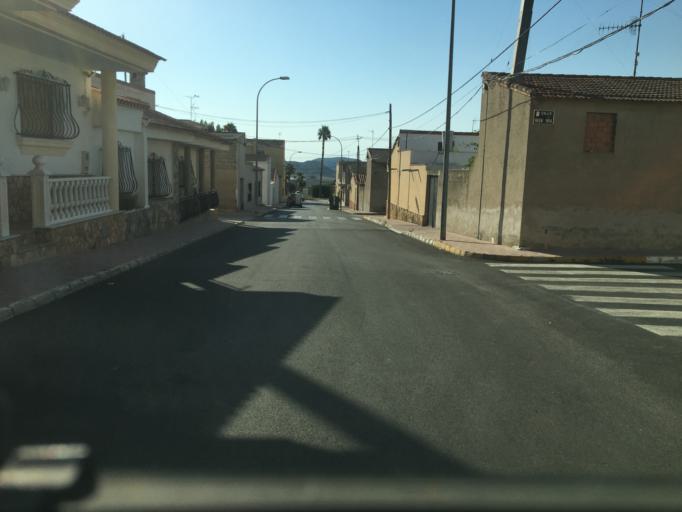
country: ES
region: Murcia
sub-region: Murcia
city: Puerto Lumbreras
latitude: 37.5521
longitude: -1.8154
